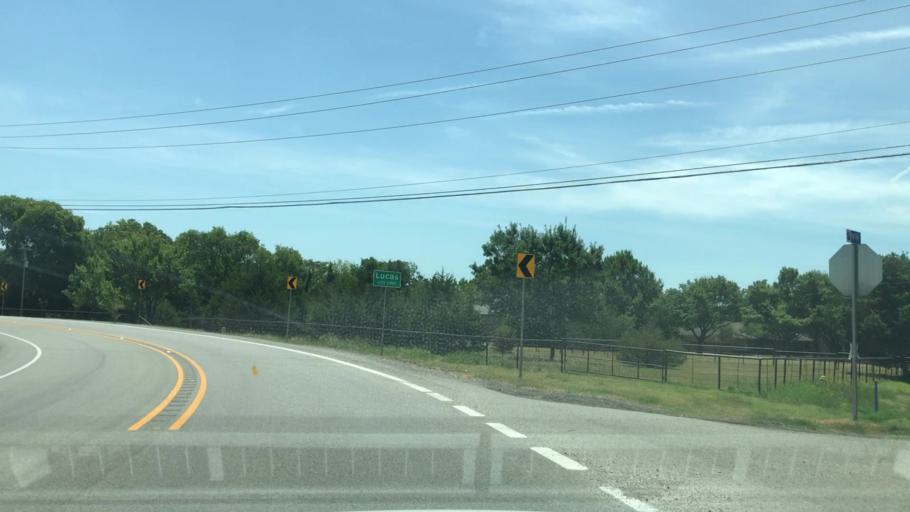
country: US
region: Texas
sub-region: Collin County
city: Fairview
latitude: 33.1202
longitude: -96.6089
